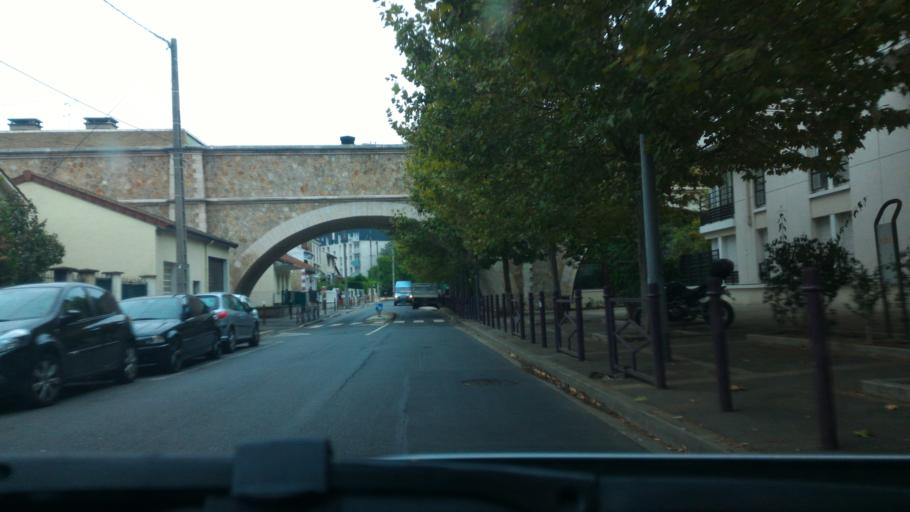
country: FR
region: Ile-de-France
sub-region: Departement du Val-de-Marne
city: Cachan
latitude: 48.7909
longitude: 2.3337
